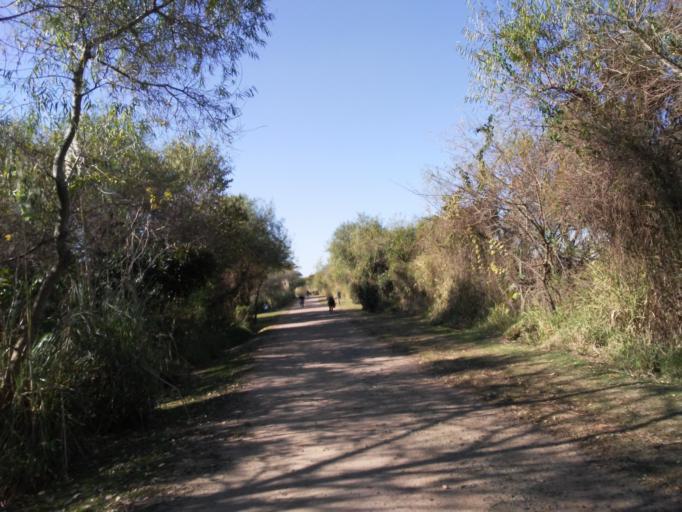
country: AR
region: Buenos Aires F.D.
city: Buenos Aires
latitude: -34.6086
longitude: -58.3551
